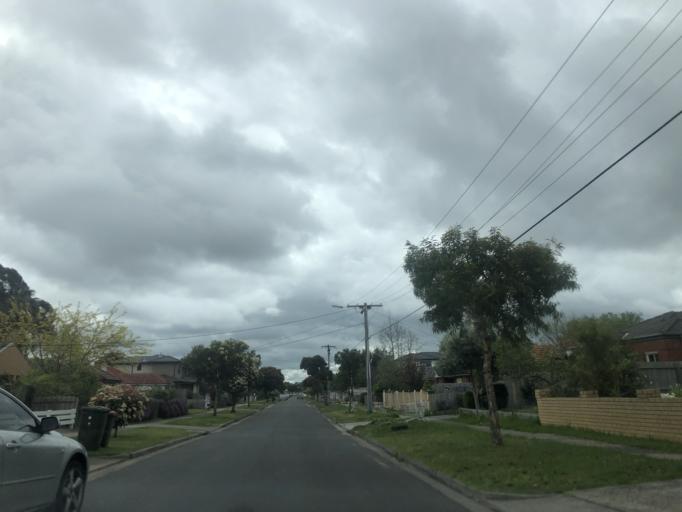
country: AU
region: Victoria
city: Clayton
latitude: -37.9232
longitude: 145.1112
